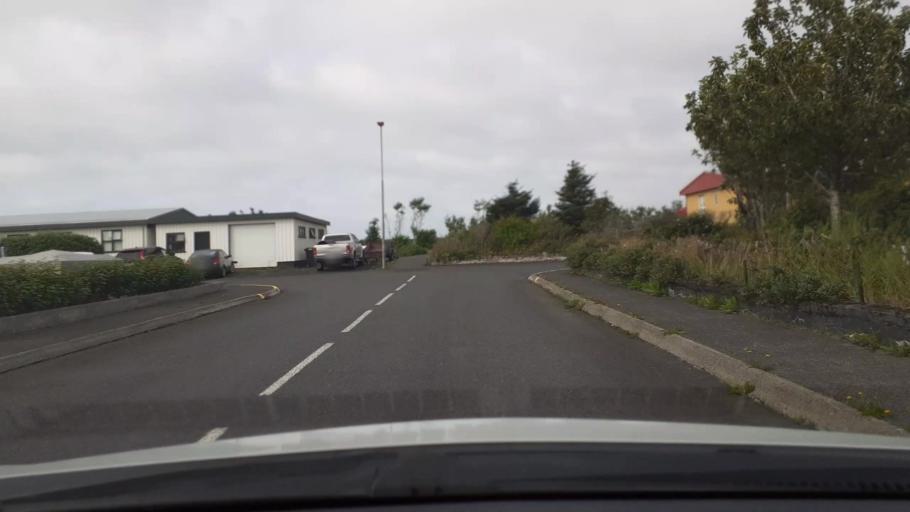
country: IS
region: South
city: THorlakshoefn
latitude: 63.8559
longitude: -21.3943
